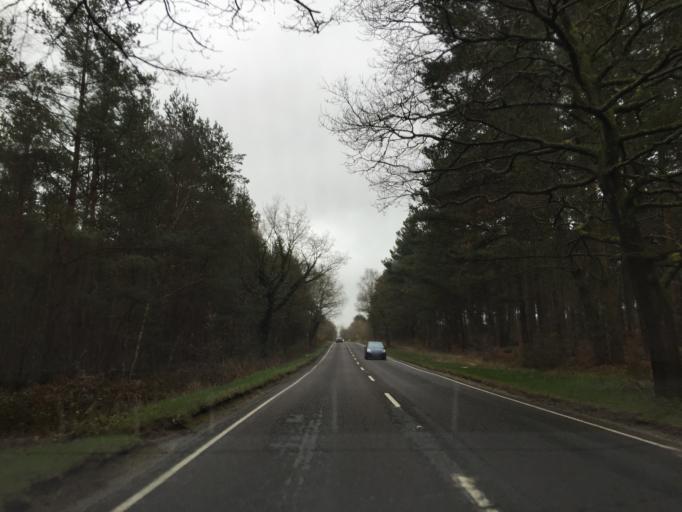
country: GB
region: England
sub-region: Hampshire
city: Ringwood
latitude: 50.8562
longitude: -1.8244
